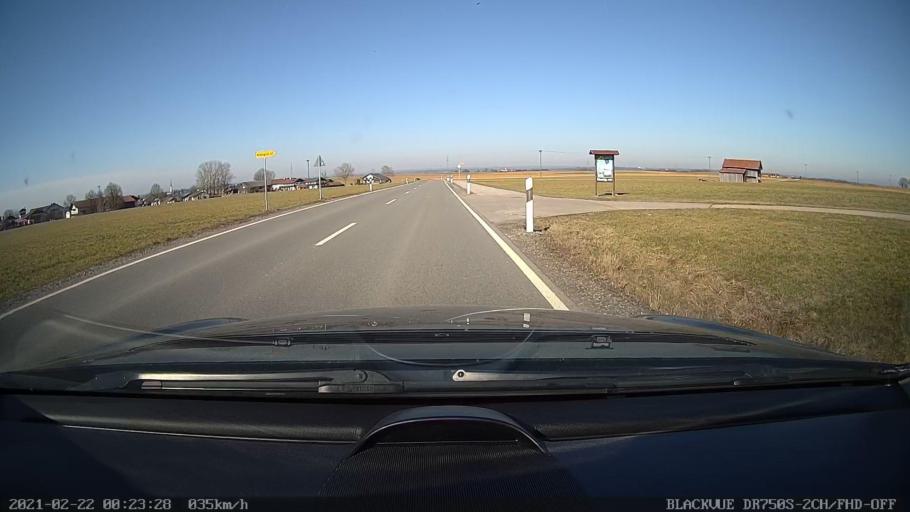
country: DE
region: Bavaria
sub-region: Upper Bavaria
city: Griesstatt
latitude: 47.9862
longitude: 12.2007
